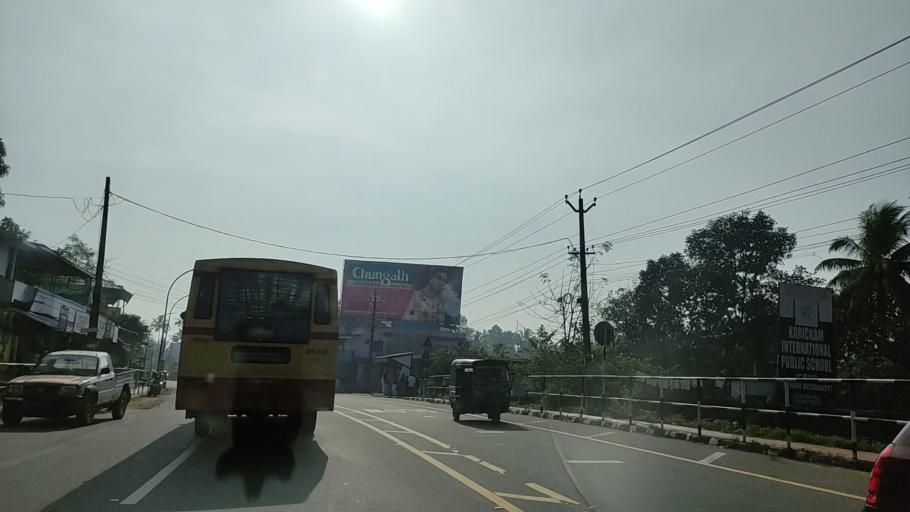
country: IN
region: Kerala
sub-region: Kollam
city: Punalur
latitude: 8.9851
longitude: 76.8027
